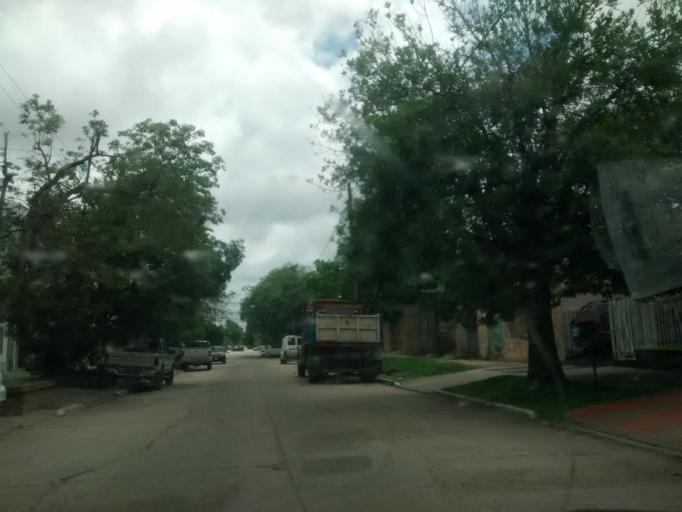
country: AR
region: Chaco
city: Resistencia
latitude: -27.4428
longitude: -58.9987
